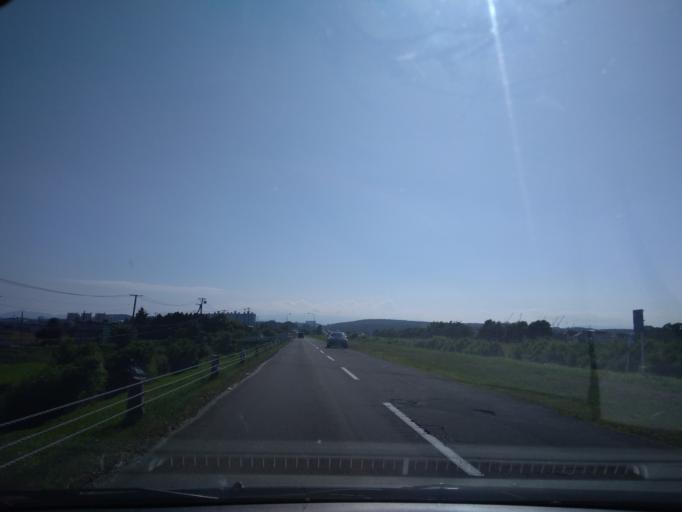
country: JP
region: Hokkaido
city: Kitahiroshima
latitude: 42.9919
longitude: 141.5794
